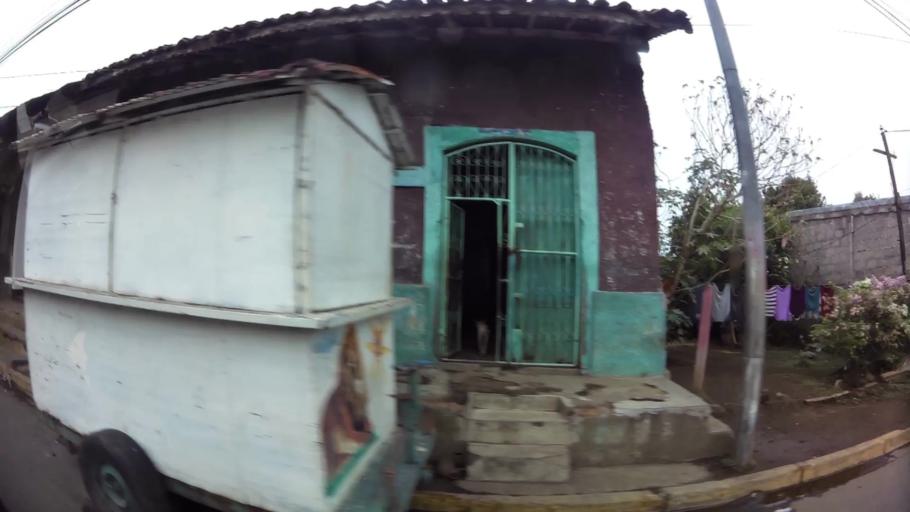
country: NI
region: Leon
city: Leon
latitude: 12.4480
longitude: -86.8743
